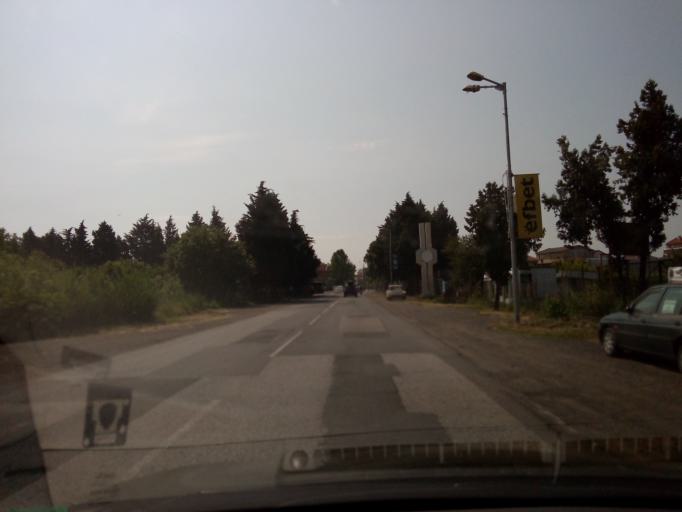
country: BG
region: Burgas
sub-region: Obshtina Pomorie
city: Pomorie
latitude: 42.5722
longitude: 27.6115
